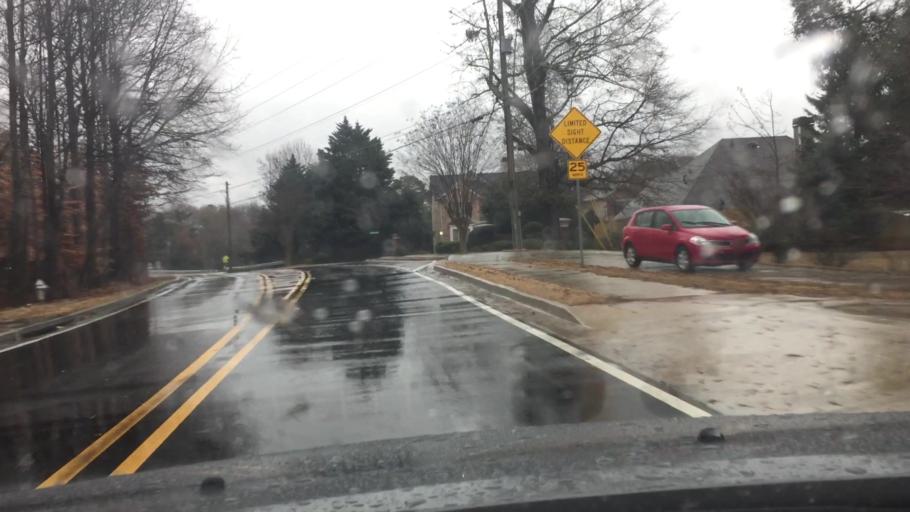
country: US
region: Georgia
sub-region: Cobb County
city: Kennesaw
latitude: 33.9902
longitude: -84.6087
